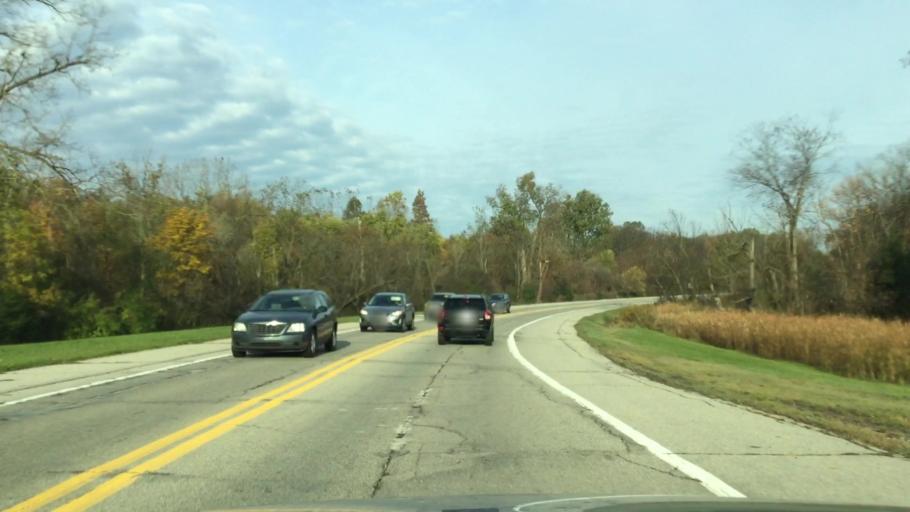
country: US
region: Michigan
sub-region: Wayne County
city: Dearborn Heights
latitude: 42.3333
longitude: -83.2562
